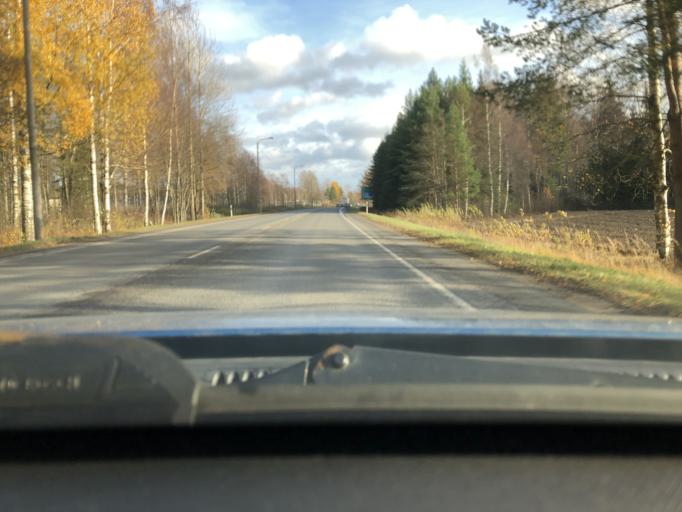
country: FI
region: Pirkanmaa
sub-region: Tampere
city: Kangasala
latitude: 61.4662
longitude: 24.0171
